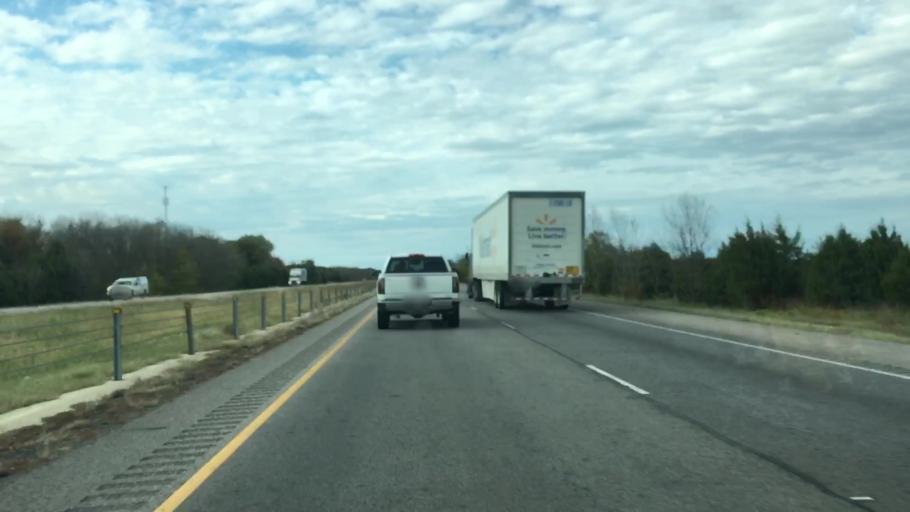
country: US
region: Arkansas
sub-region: Conway County
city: Morrilton
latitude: 35.2016
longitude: -92.8071
